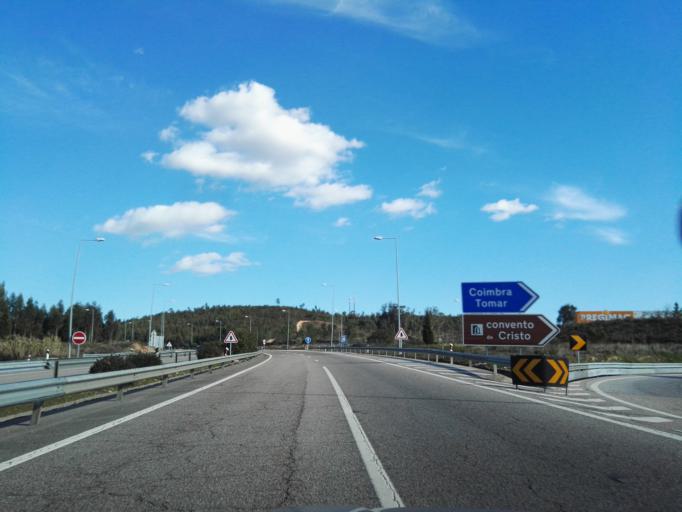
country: PT
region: Santarem
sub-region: Entroncamento
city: Entroncamento
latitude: 39.4885
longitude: -8.4471
